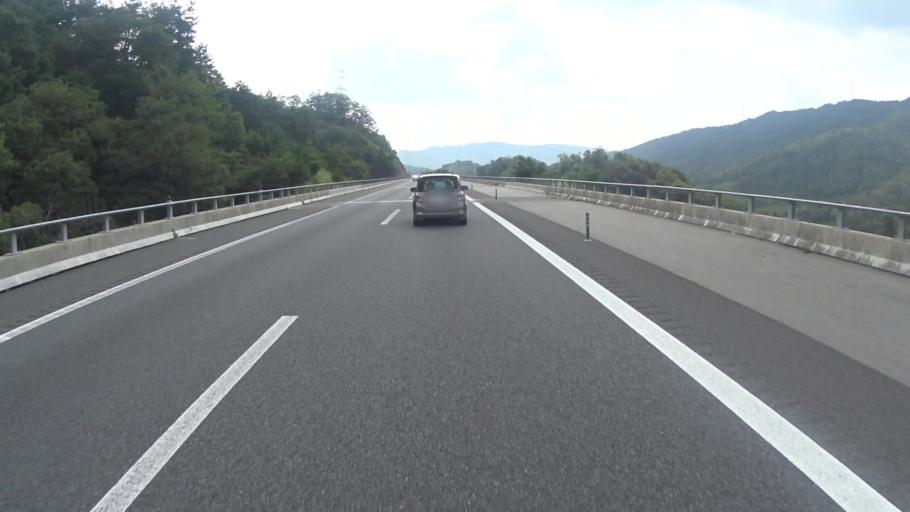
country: JP
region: Shiga Prefecture
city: Kusatsu
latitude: 34.9327
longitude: 136.0474
